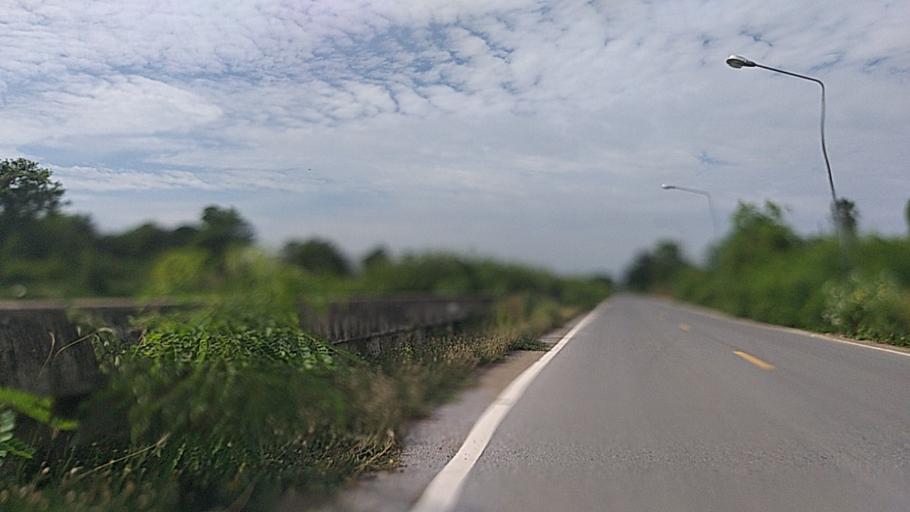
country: TH
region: Pathum Thani
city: Nong Suea
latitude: 14.0399
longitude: 100.8931
